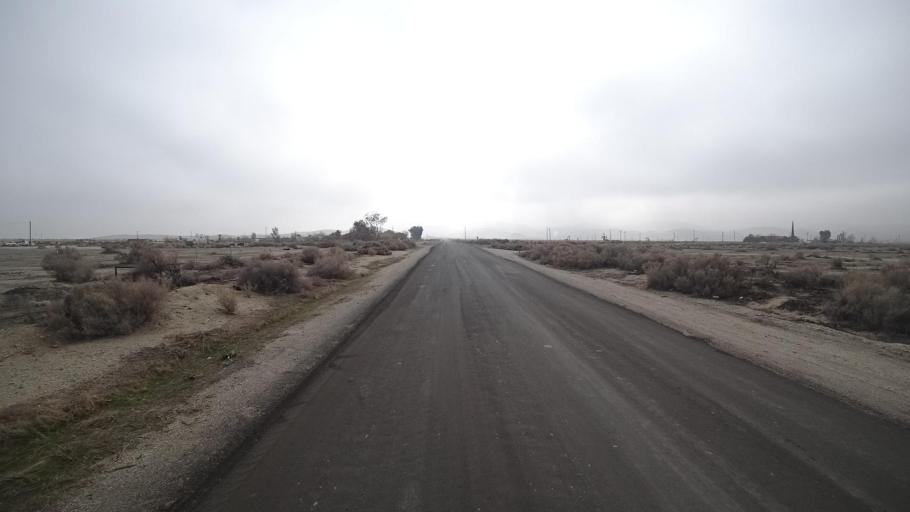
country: US
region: California
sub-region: Kern County
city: Maricopa
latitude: 35.0497
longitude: -119.3670
